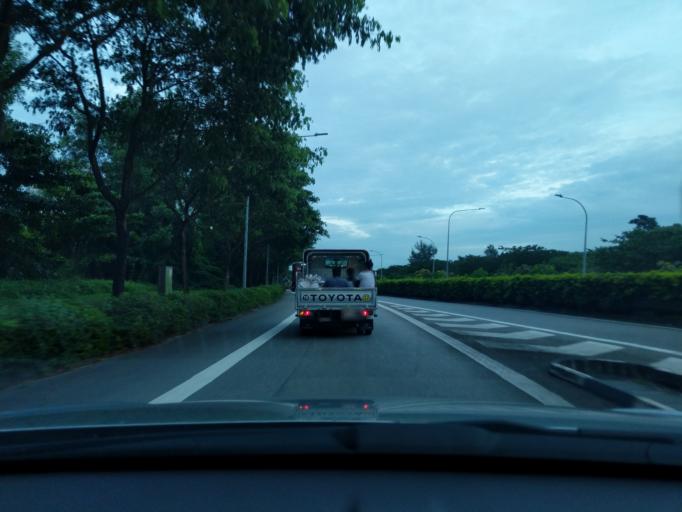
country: SG
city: Singapore
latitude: 1.2960
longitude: 103.8786
